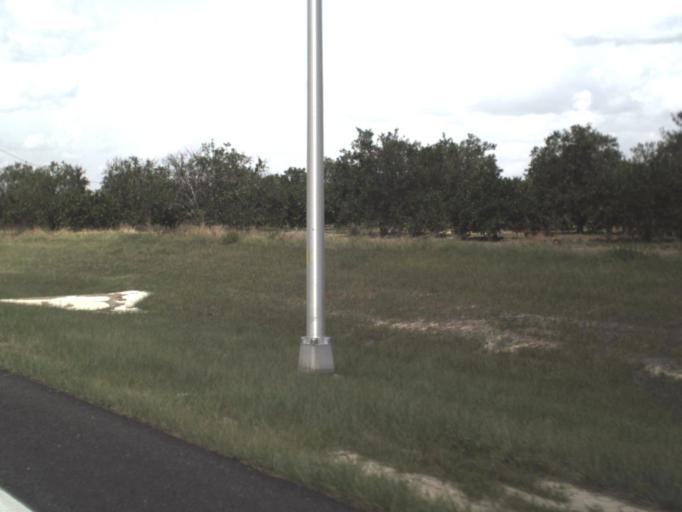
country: US
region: Florida
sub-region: Highlands County
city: Avon Park
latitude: 27.6376
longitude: -81.5217
